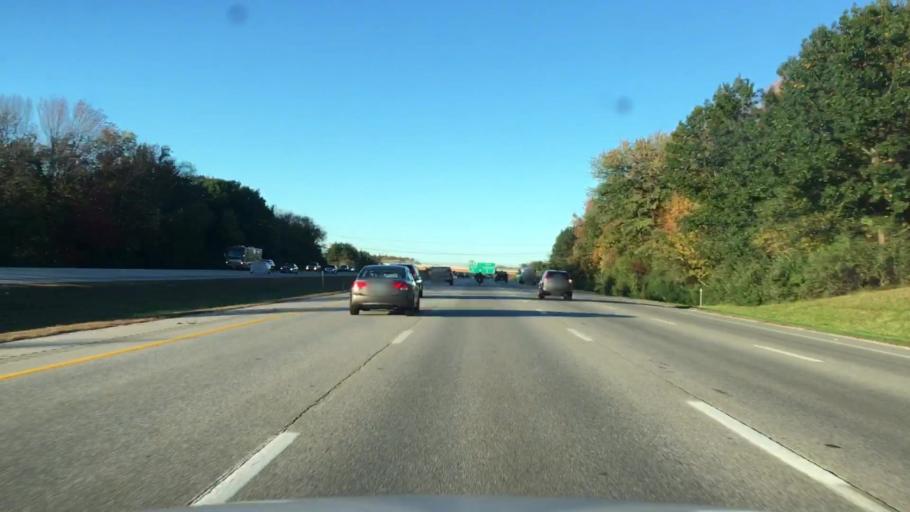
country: US
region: New Hampshire
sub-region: Rockingham County
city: Greenland
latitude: 43.0384
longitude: -70.8189
